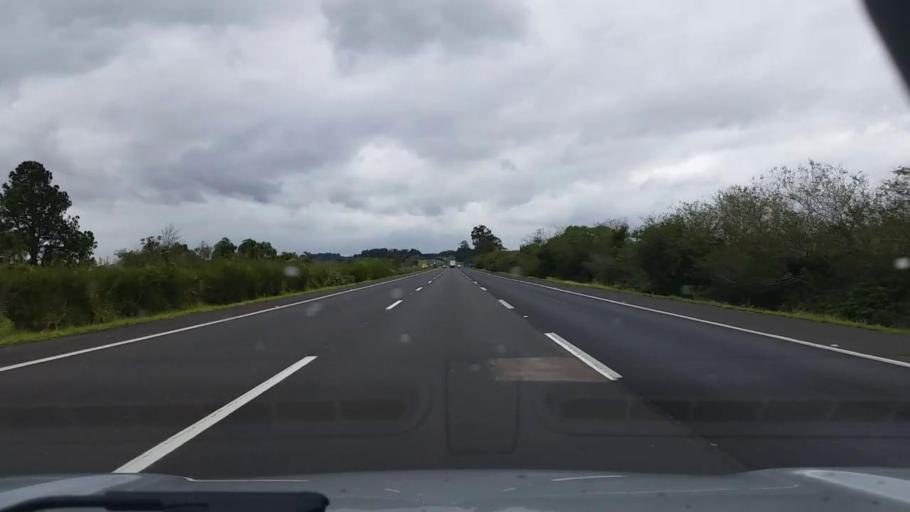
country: BR
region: Rio Grande do Sul
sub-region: Gravatai
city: Gravatai
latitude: -29.9211
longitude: -50.8398
